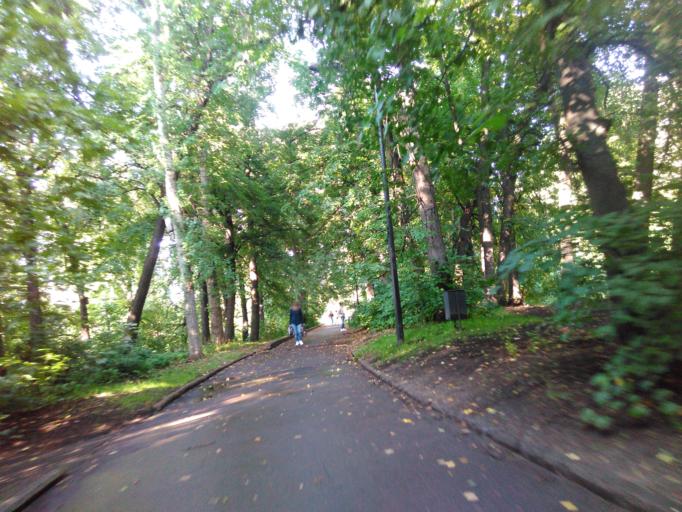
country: RU
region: Moskovskaya
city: Leninskiye Gory
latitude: 55.7099
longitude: 37.5684
